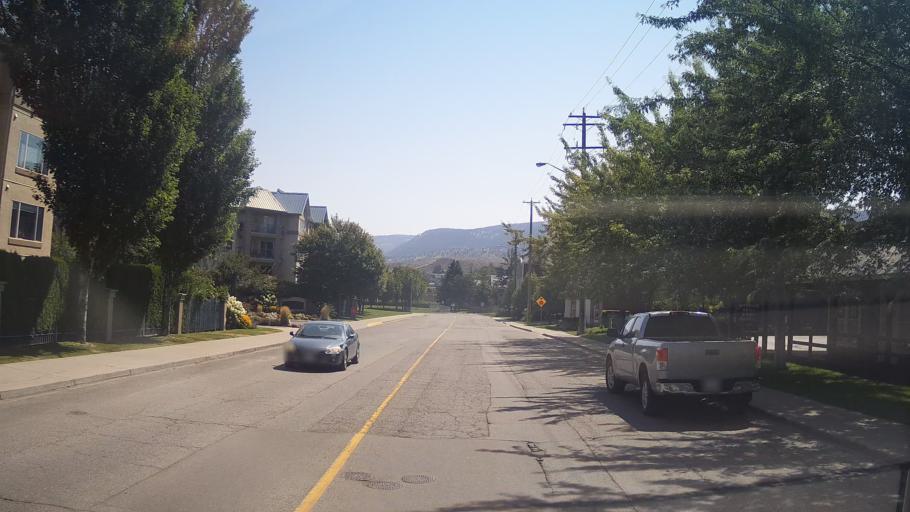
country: CA
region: British Columbia
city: Kamloops
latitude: 50.6761
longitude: -120.3180
